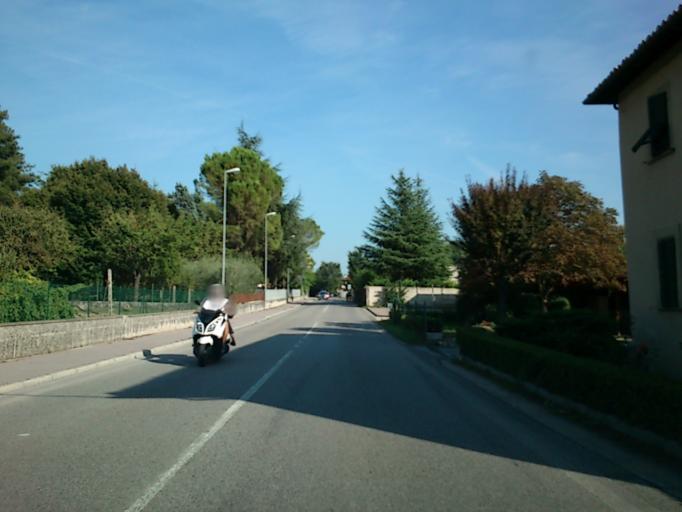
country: IT
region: The Marches
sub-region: Provincia di Pesaro e Urbino
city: Canavaccio
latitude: 43.6952
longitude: 12.6973
